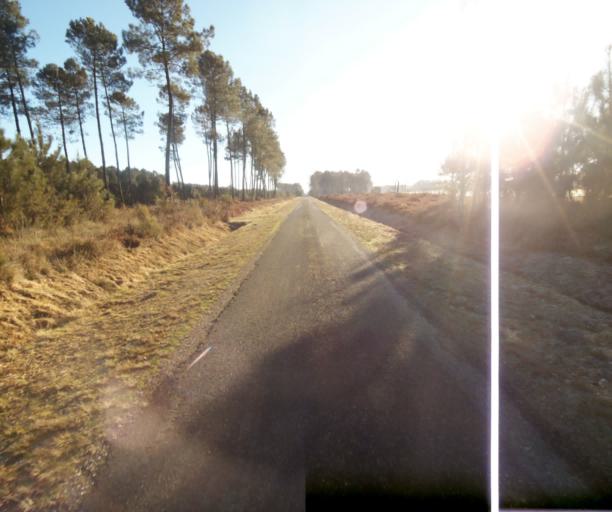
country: FR
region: Aquitaine
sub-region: Departement des Landes
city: Gabarret
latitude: 44.1135
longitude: 0.0415
